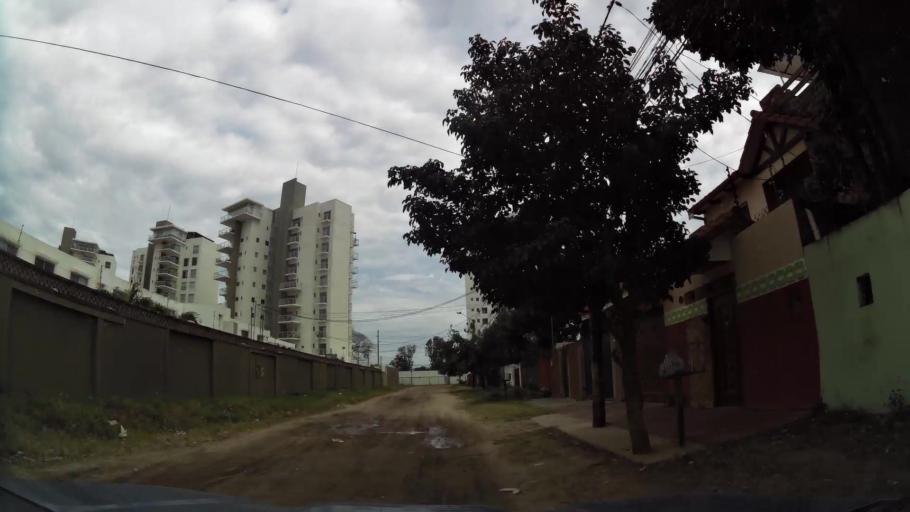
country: BO
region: Santa Cruz
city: Santa Cruz de la Sierra
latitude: -17.7383
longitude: -63.1796
